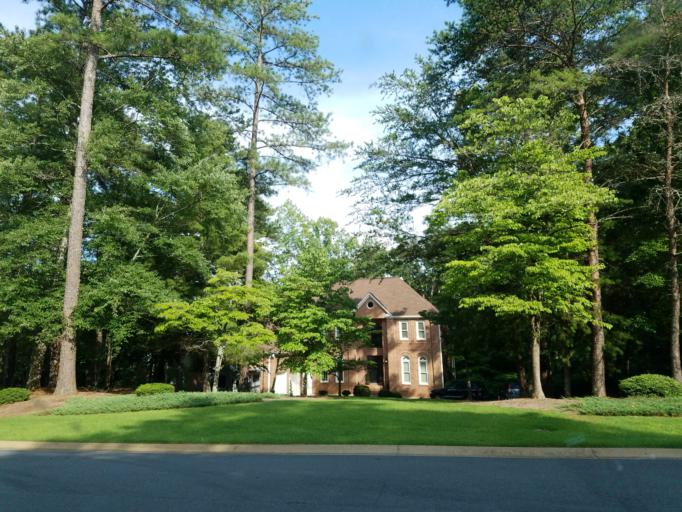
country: US
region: Georgia
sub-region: Cobb County
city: Vinings
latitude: 33.9250
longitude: -84.4512
